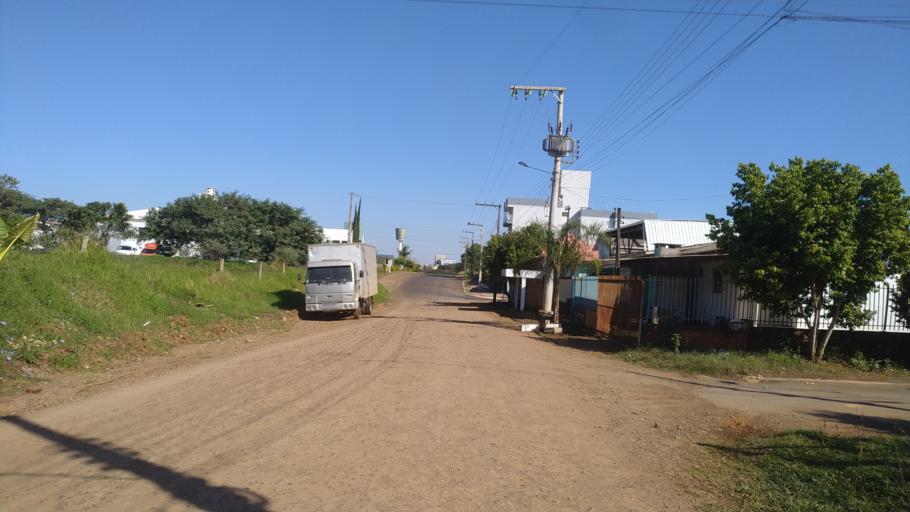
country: BR
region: Santa Catarina
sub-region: Chapeco
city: Chapeco
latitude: -27.0853
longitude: -52.6020
